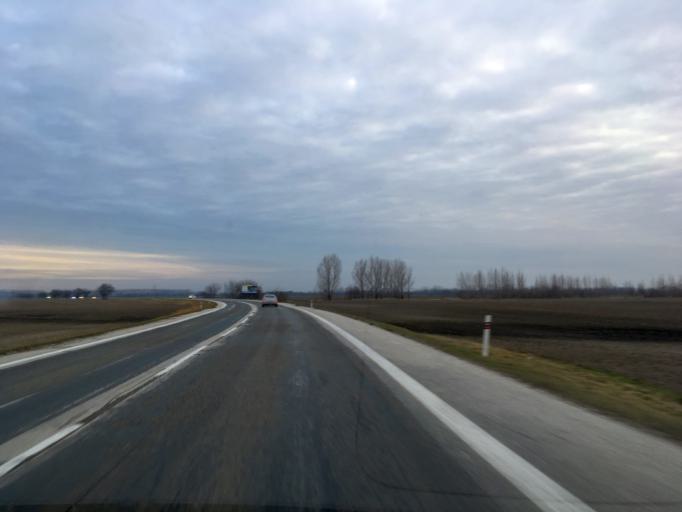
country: SK
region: Trnavsky
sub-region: Okres Dunajska Streda
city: Velky Meder
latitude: 47.9285
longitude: 17.7228
